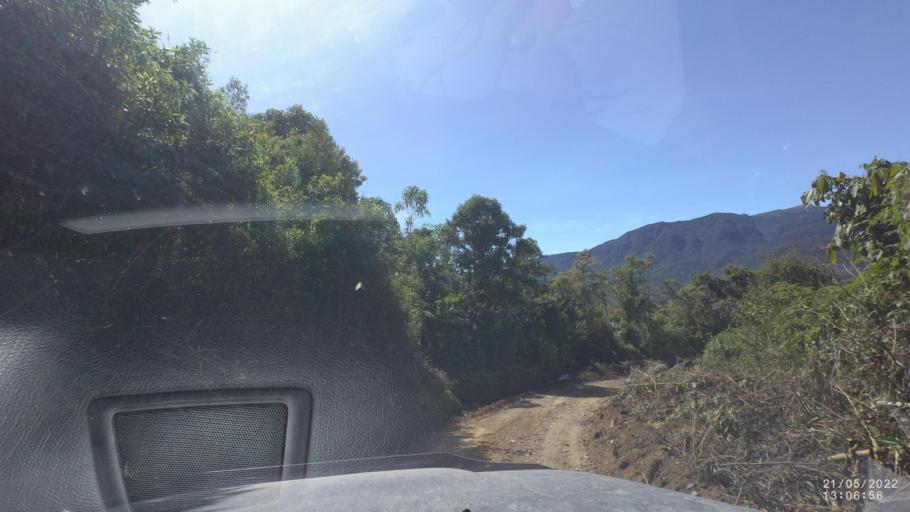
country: BO
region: Cochabamba
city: Colomi
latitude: -17.1518
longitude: -65.9465
